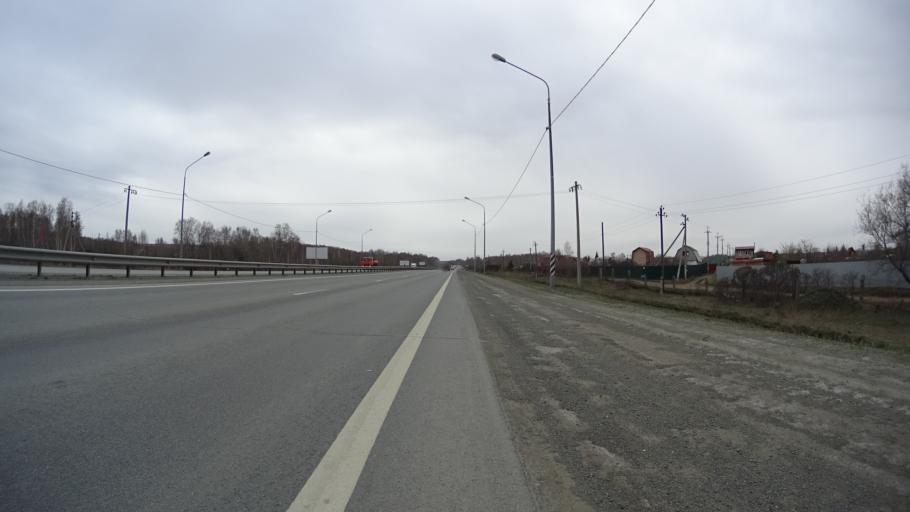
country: RU
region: Chelyabinsk
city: Novosineglazovskiy
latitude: 54.9788
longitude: 61.4138
